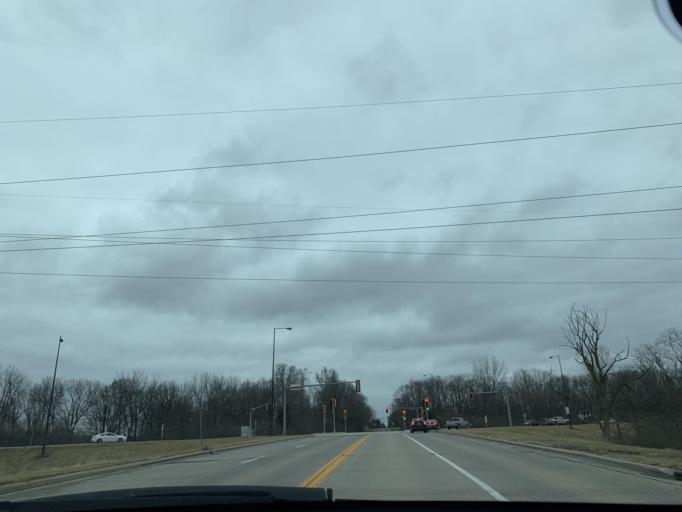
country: US
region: Illinois
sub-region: Sangamon County
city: Leland Grove
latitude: 39.8242
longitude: -89.6873
